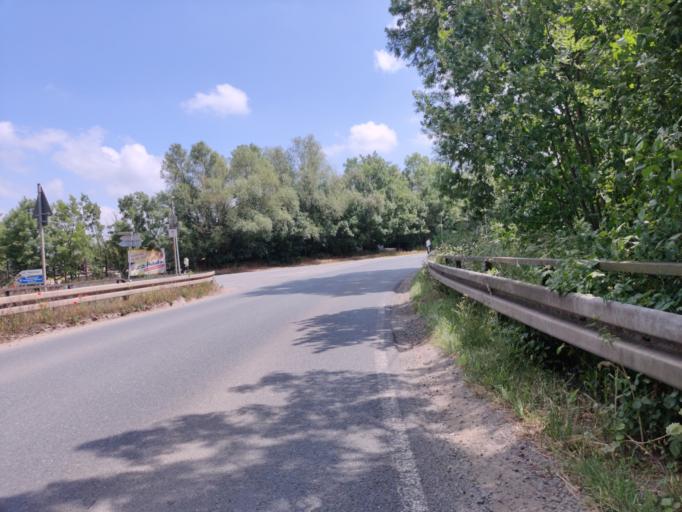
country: DE
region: Lower Saxony
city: Hildesheim
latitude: 52.1709
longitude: 9.9260
